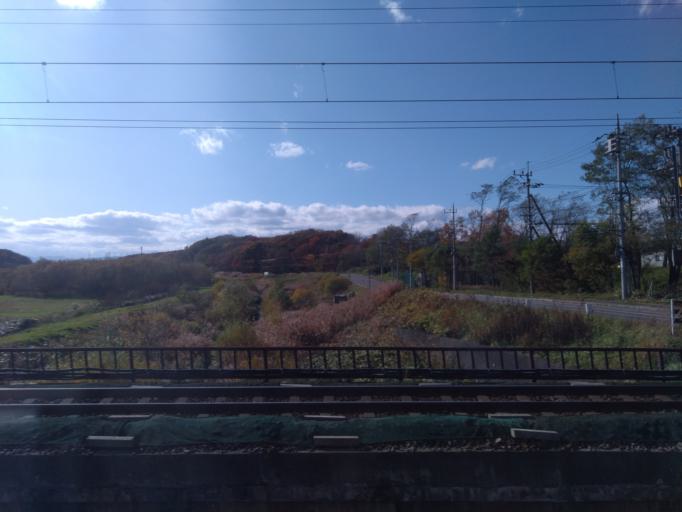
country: JP
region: Hokkaido
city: Kitahiroshima
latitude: 42.9680
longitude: 141.5667
